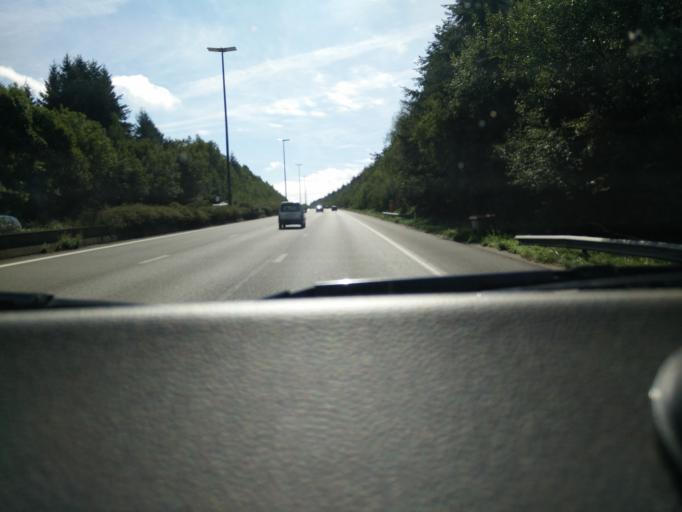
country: BE
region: Wallonia
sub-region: Province du Luxembourg
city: Tellin
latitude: 50.0709
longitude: 5.1841
